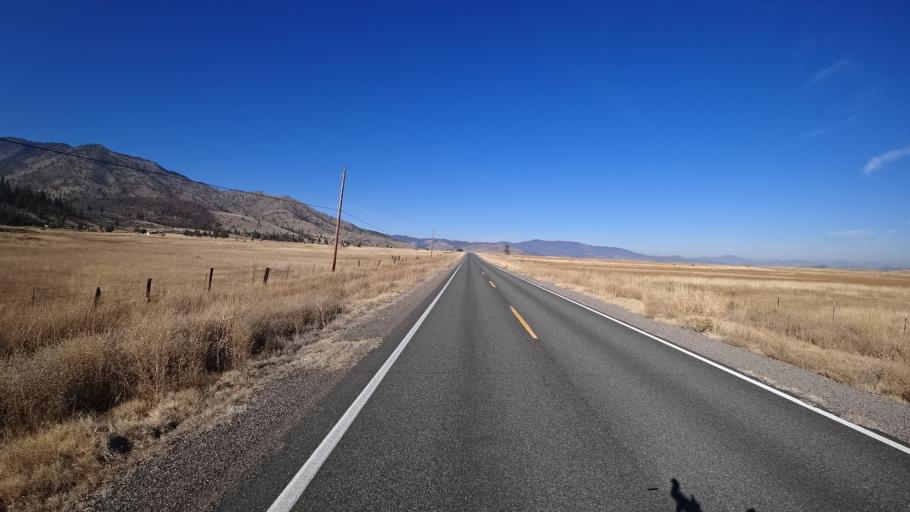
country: US
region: California
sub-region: Siskiyou County
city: Weed
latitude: 41.4721
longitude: -122.4804
